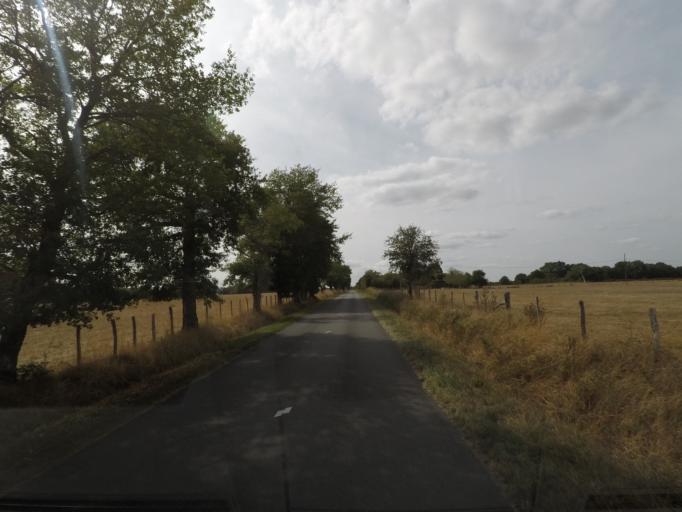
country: FR
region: Poitou-Charentes
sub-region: Departement de la Charente
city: Saint-Claud
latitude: 45.9421
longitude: 0.5191
